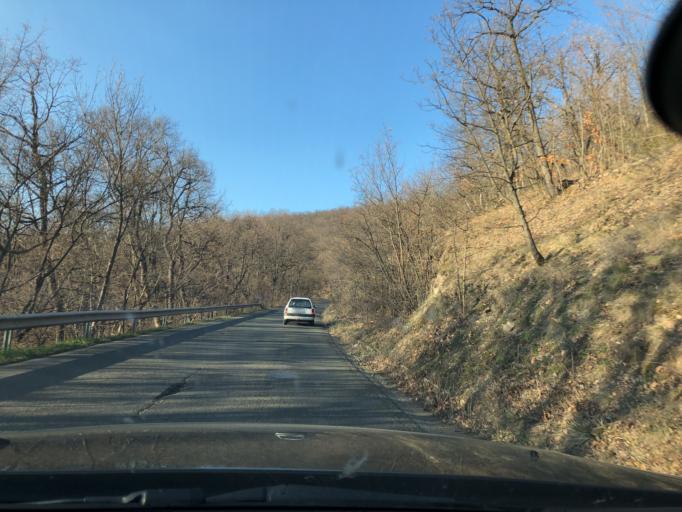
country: HU
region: Nograd
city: Paszto
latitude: 47.9265
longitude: 19.6291
